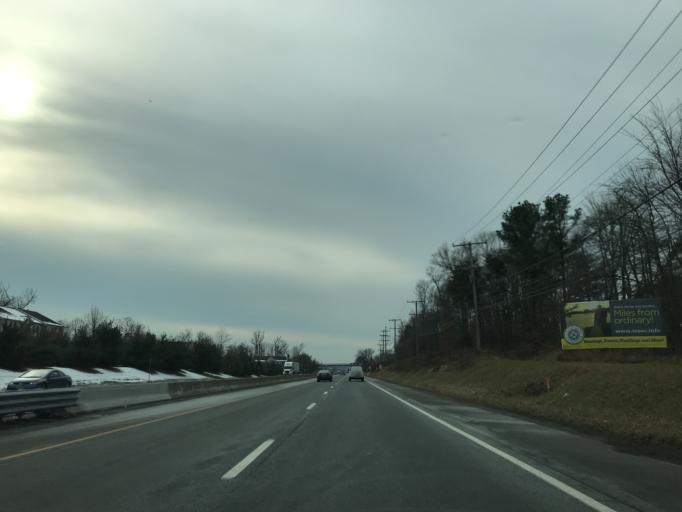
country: US
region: Maryland
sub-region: Harford County
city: Riverside
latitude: 39.4744
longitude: -76.2280
